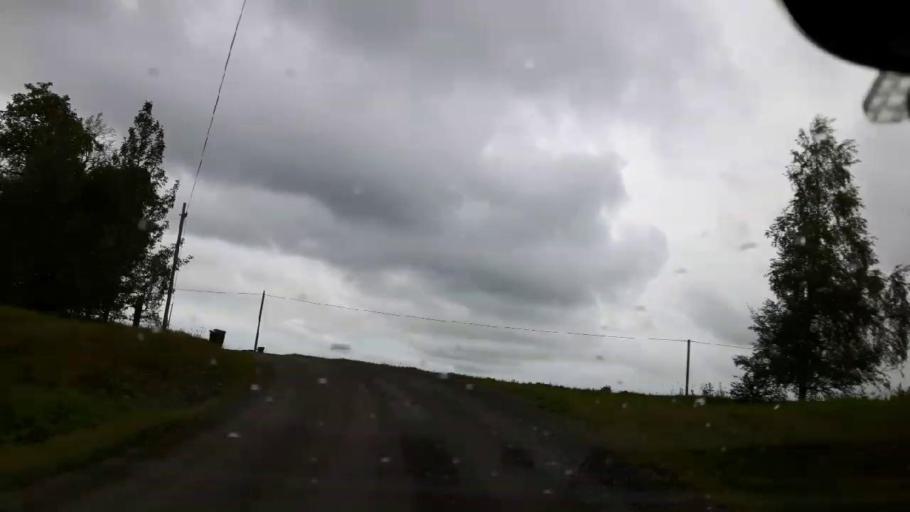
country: SE
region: Jaemtland
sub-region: OEstersunds Kommun
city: Ostersund
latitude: 63.0305
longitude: 14.5821
